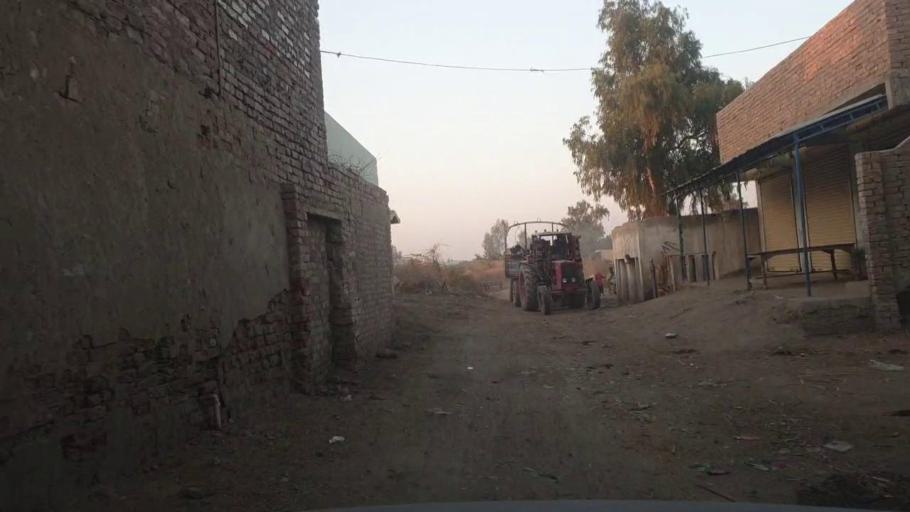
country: PK
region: Sindh
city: Chambar
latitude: 25.2965
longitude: 68.9075
